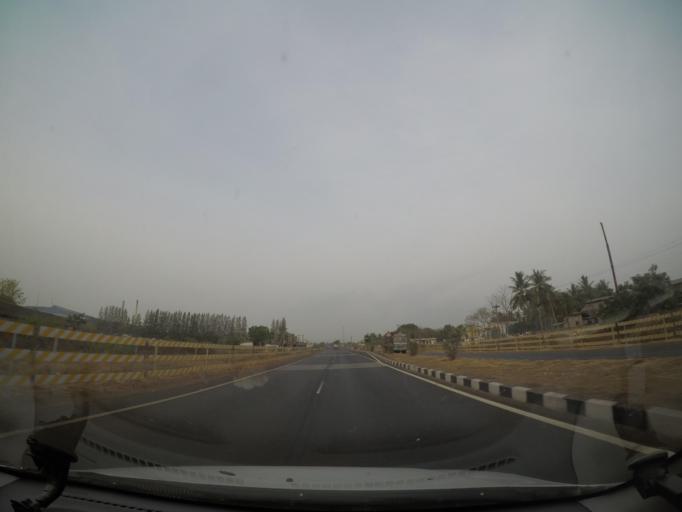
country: IN
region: Andhra Pradesh
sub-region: Krishna
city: Gannavaram
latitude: 16.6034
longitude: 80.9003
